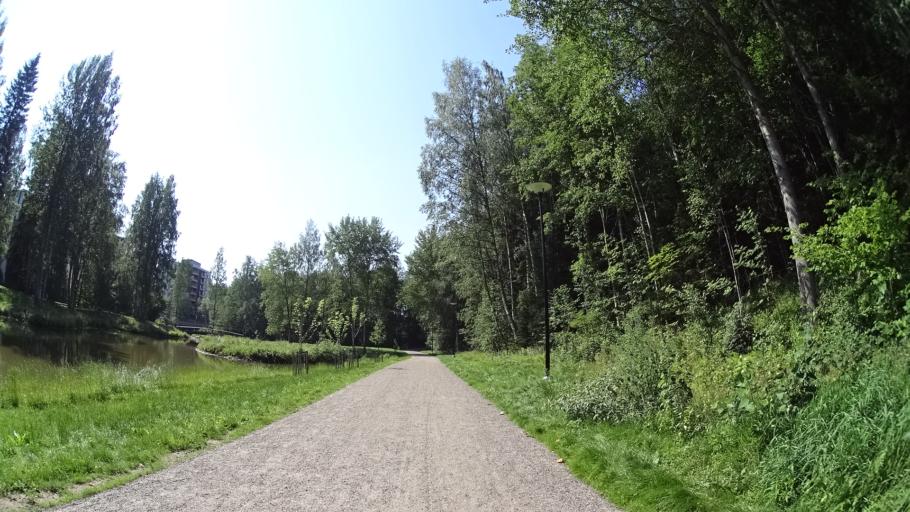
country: FI
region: Uusimaa
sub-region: Helsinki
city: Kerava
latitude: 60.3533
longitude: 25.0718
